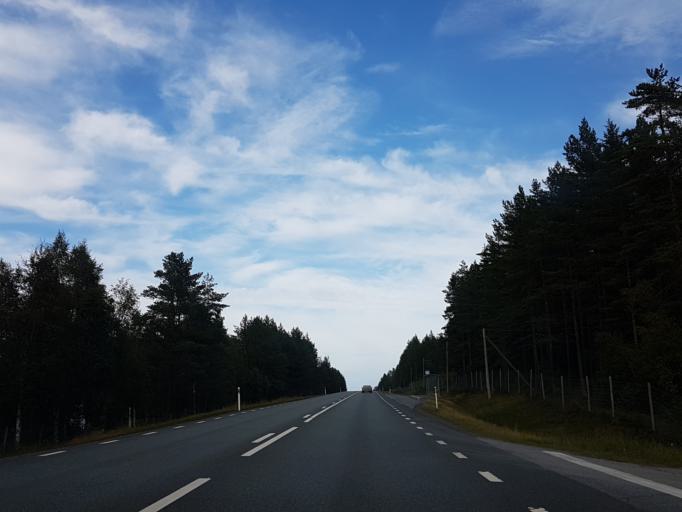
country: SE
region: Vaesterbotten
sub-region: Robertsfors Kommun
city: Robertsfors
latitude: 64.0135
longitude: 20.8203
